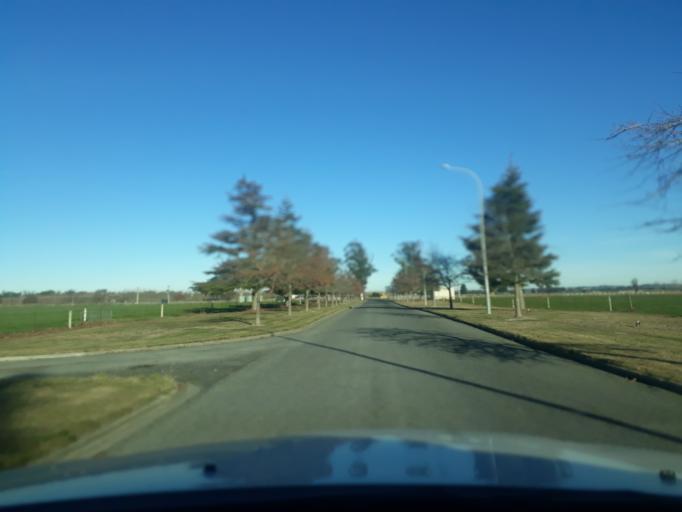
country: NZ
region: Canterbury
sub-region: Timaru District
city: Timaru
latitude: -44.3076
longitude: 171.2258
